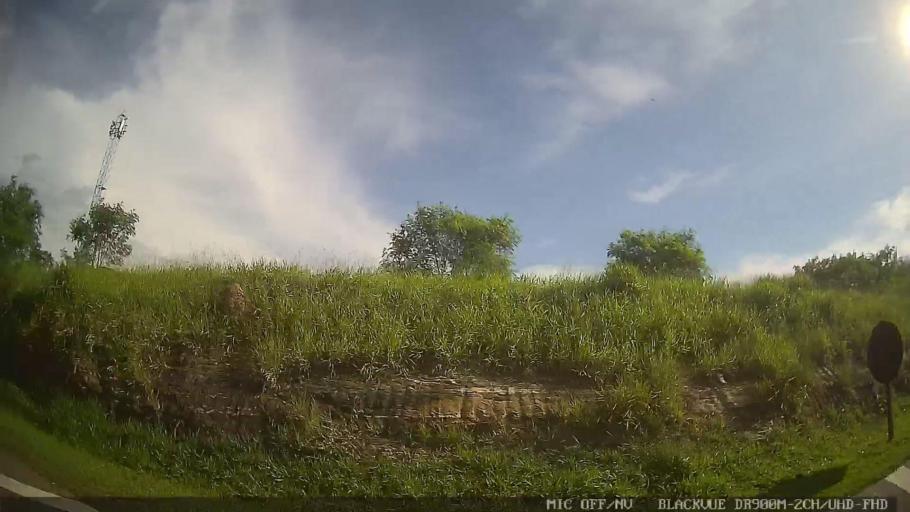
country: BR
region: Sao Paulo
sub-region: Tiete
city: Tiete
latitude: -23.1183
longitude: -47.7161
